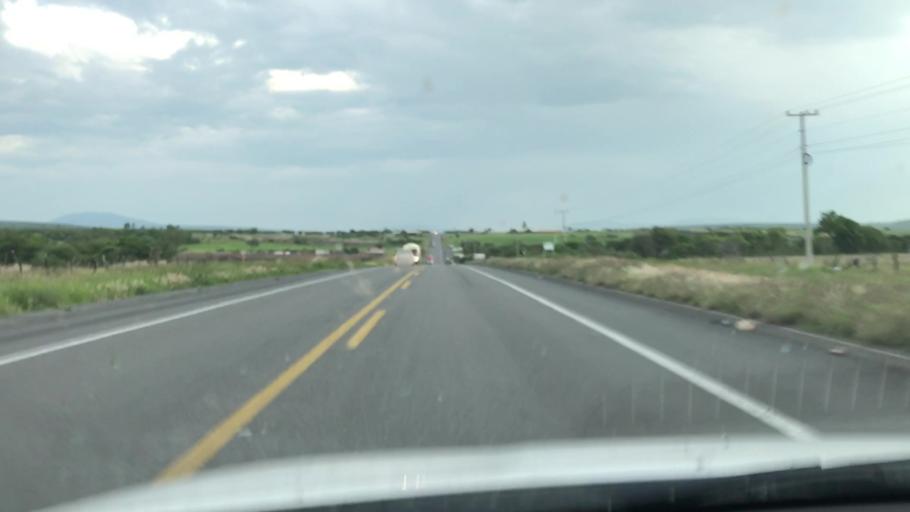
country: MX
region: Jalisco
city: Degollado
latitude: 20.3589
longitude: -102.1502
